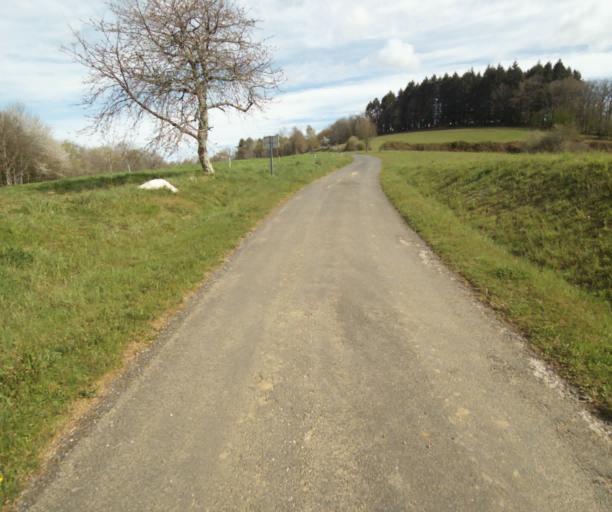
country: FR
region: Limousin
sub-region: Departement de la Correze
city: Laguenne
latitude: 45.2538
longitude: 1.8072
